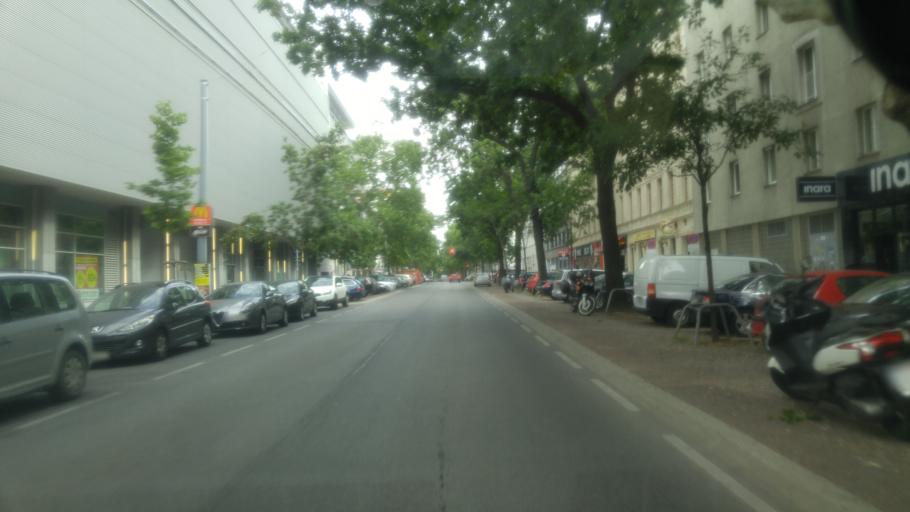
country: AT
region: Vienna
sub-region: Wien Stadt
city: Vienna
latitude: 48.2407
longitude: 16.3843
